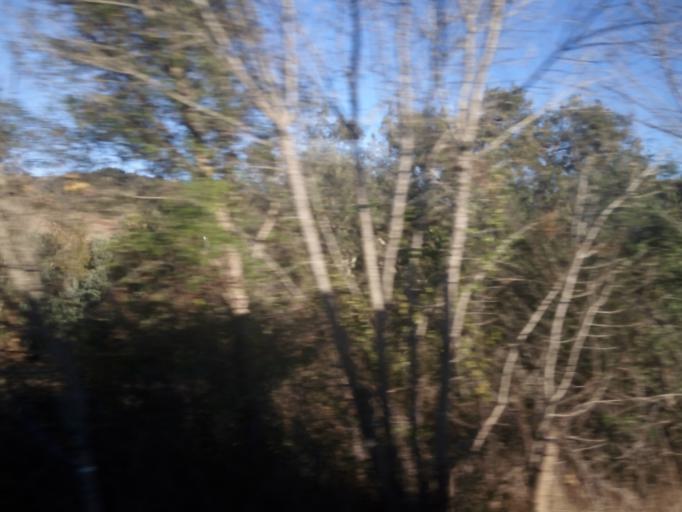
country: PT
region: Beja
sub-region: Odemira
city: Odemira
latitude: 37.5782
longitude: -8.4921
